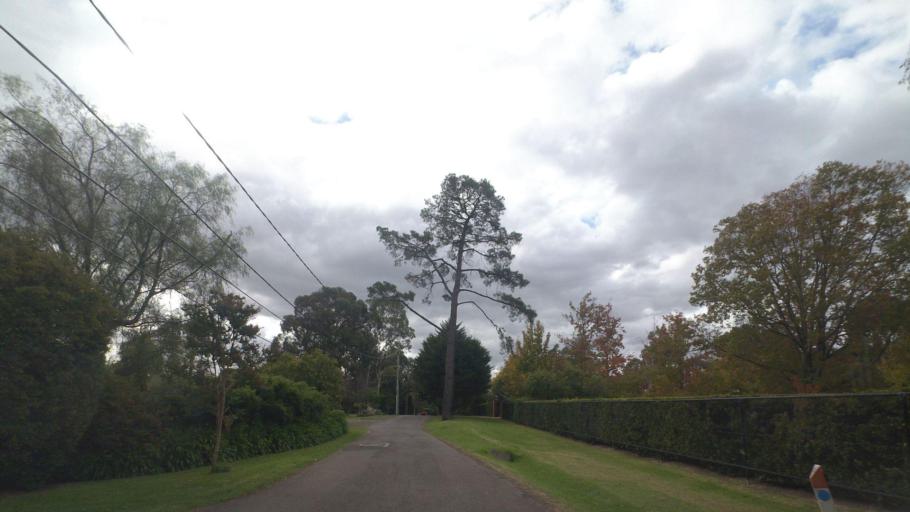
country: AU
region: Victoria
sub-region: Nillumbik
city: Eltham
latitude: -37.7557
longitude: 145.1517
